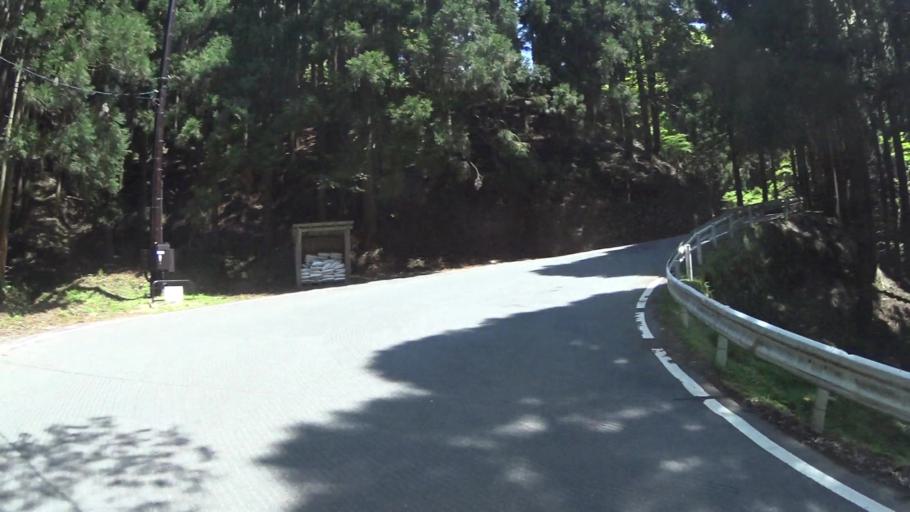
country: JP
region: Shiga Prefecture
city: Kitahama
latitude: 35.1559
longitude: 135.7894
